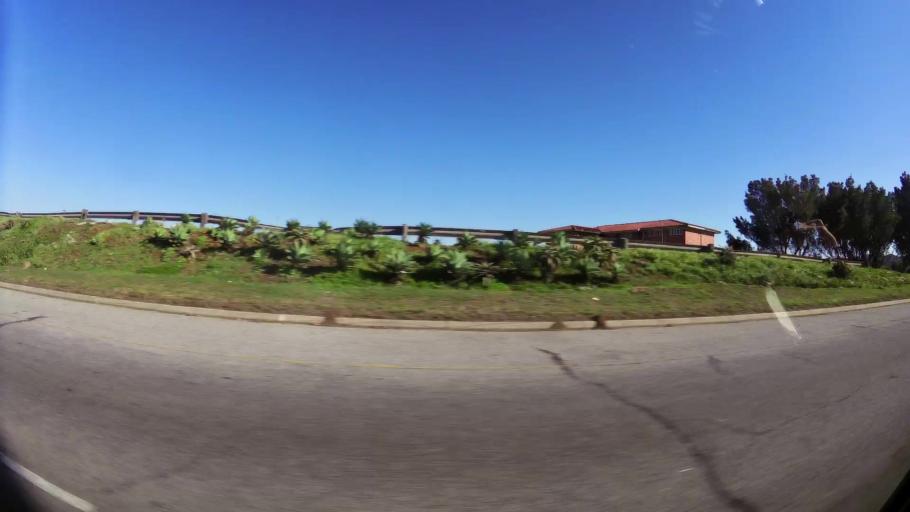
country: ZA
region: Eastern Cape
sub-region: Nelson Mandela Bay Metropolitan Municipality
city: Port Elizabeth
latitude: -33.9299
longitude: 25.6096
